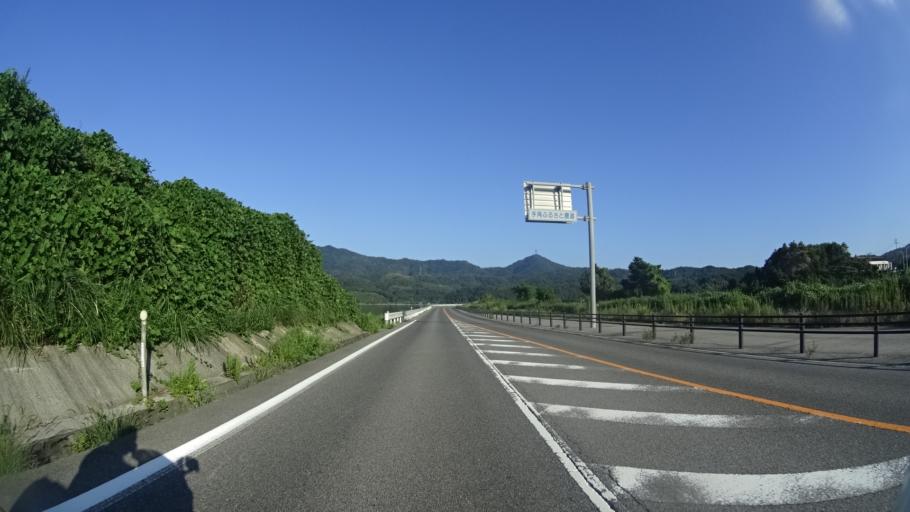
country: JP
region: Shimane
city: Sakaiminato
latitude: 35.5313
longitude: 133.1625
